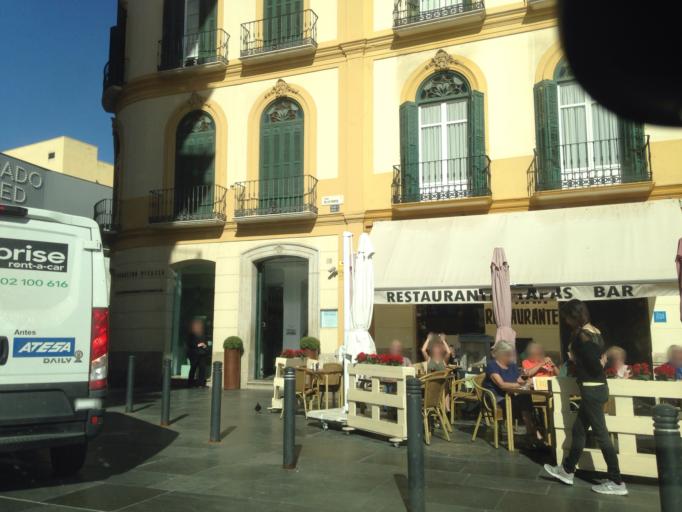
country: ES
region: Andalusia
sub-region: Provincia de Malaga
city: Malaga
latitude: 36.7238
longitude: -4.4176
